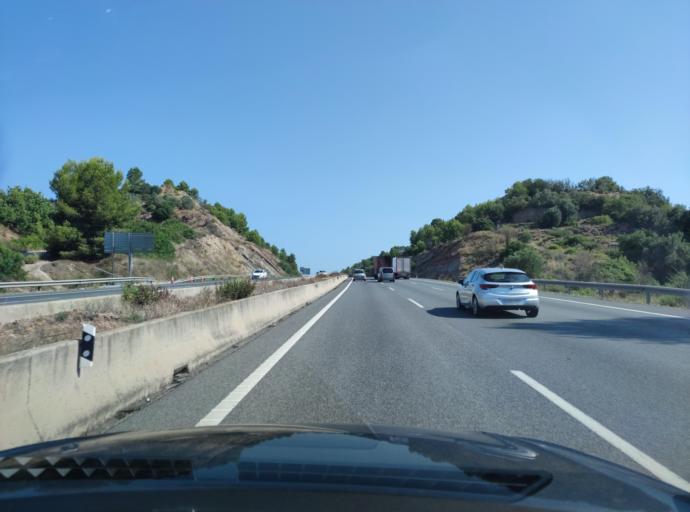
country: ES
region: Valencia
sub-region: Provincia de Valencia
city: Llosa de Ranes
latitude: 39.0294
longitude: -0.5514
